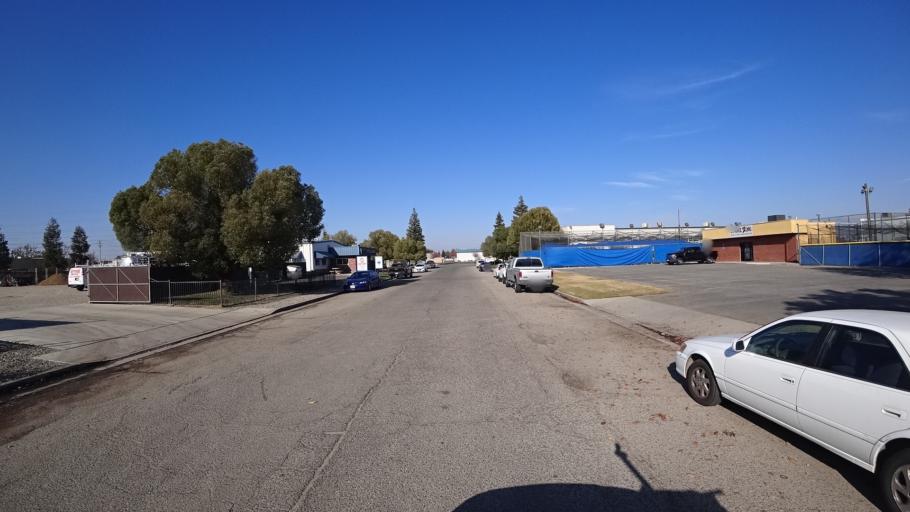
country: US
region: California
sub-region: Kern County
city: Greenacres
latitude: 35.3913
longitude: -119.0903
